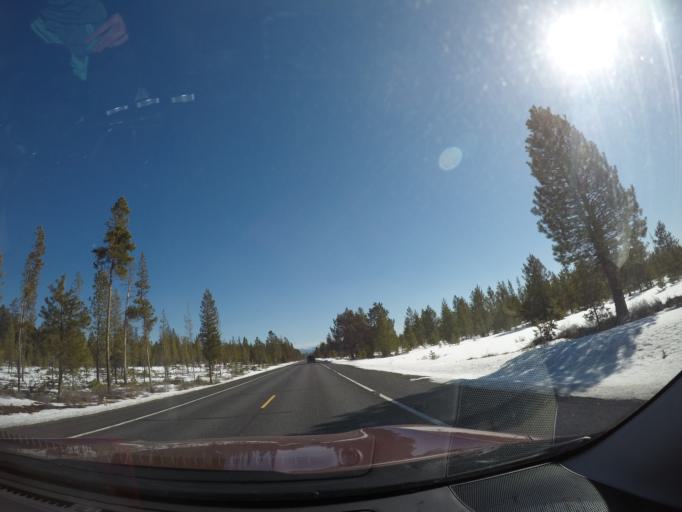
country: US
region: Oregon
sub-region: Deschutes County
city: Three Rivers
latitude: 43.8606
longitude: -121.5287
